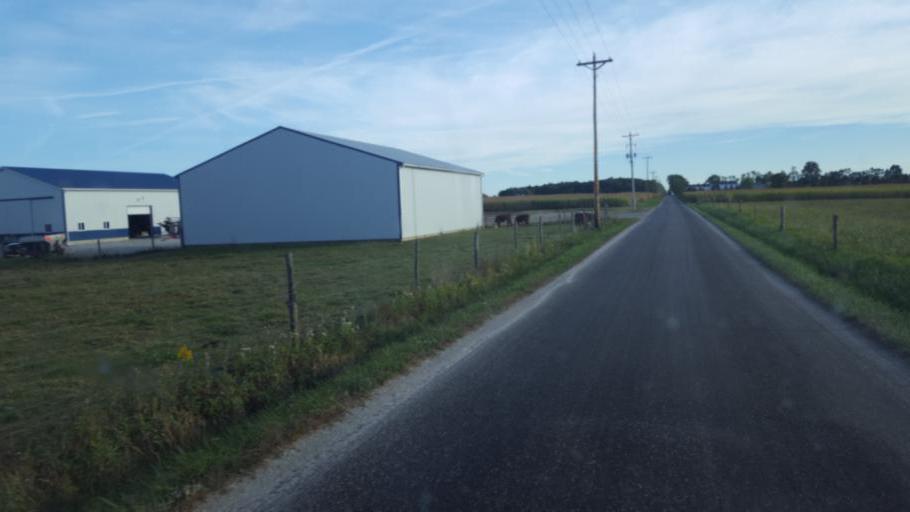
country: US
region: Ohio
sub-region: Ashland County
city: Ashland
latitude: 40.8770
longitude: -82.3877
